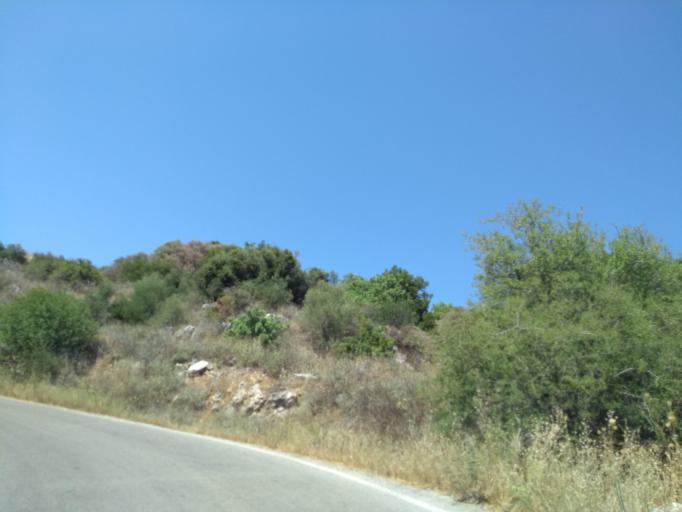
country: GR
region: Crete
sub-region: Nomos Chanias
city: Georgioupolis
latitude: 35.3829
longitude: 24.2362
